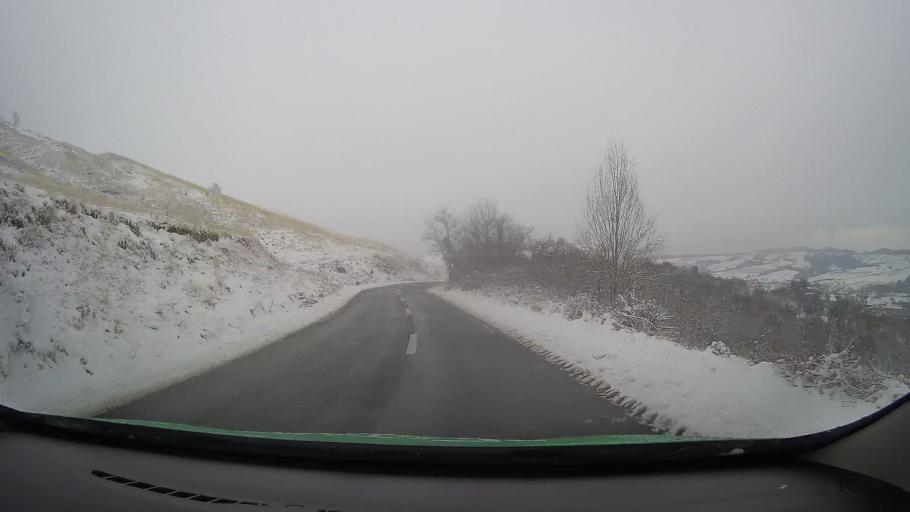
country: RO
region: Hunedoara
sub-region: Comuna Unirea
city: Unirea
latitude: 45.6597
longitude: 22.9161
